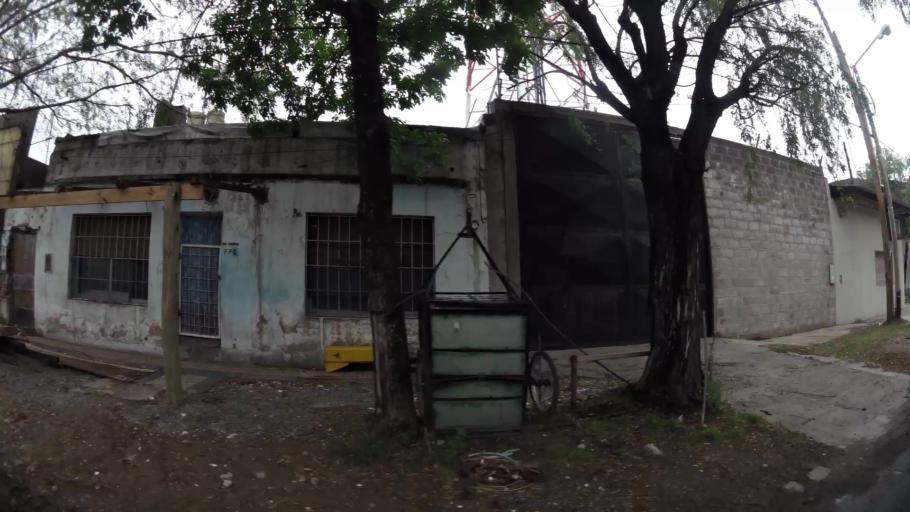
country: AR
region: Buenos Aires
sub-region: Partido de Lanus
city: Lanus
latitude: -34.7106
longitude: -58.3630
